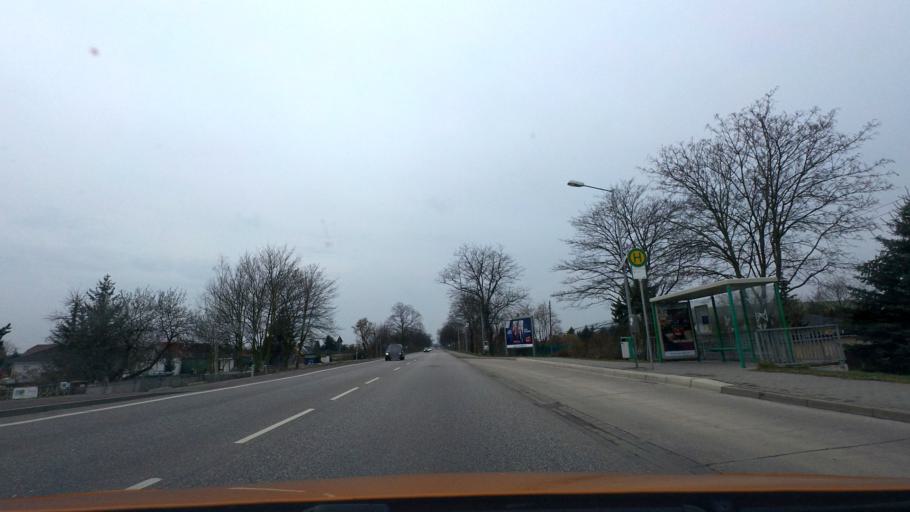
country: DE
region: Saxony-Anhalt
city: Biederitz
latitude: 52.1325
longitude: 11.6934
